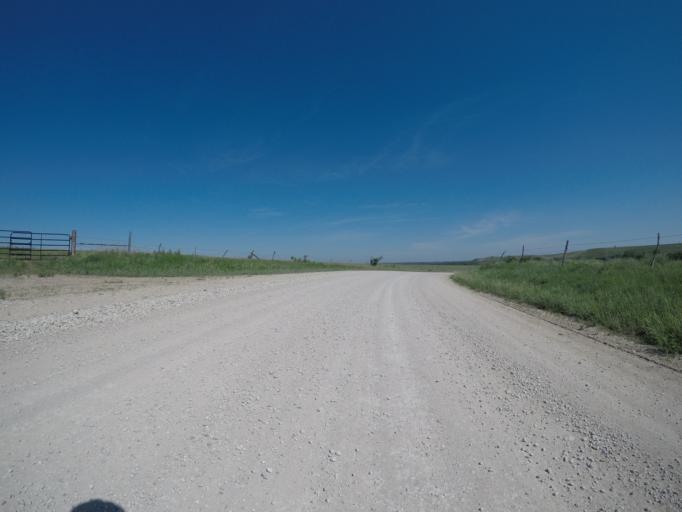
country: US
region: Kansas
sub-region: Wabaunsee County
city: Alma
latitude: 39.0157
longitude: -96.1412
